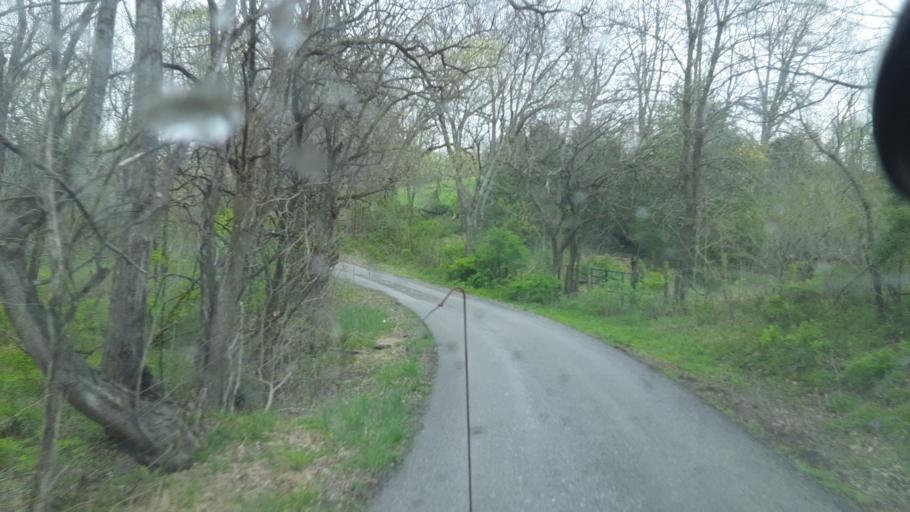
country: US
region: Kentucky
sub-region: Owen County
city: Owenton
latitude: 38.6417
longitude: -84.7785
